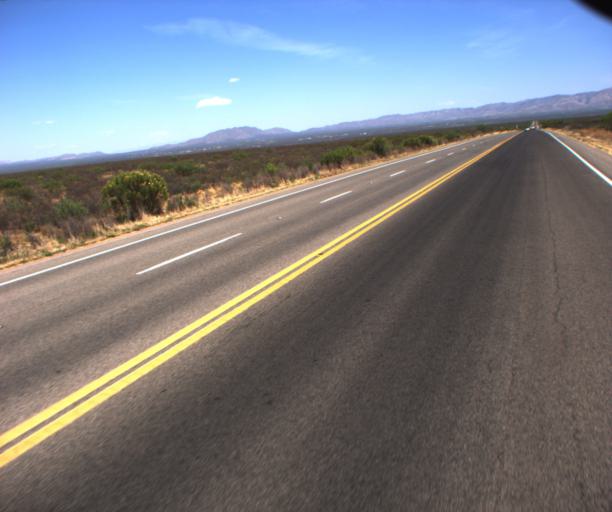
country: US
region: Arizona
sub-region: Cochise County
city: Sierra Vista Southeast
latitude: 31.5511
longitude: -110.1865
